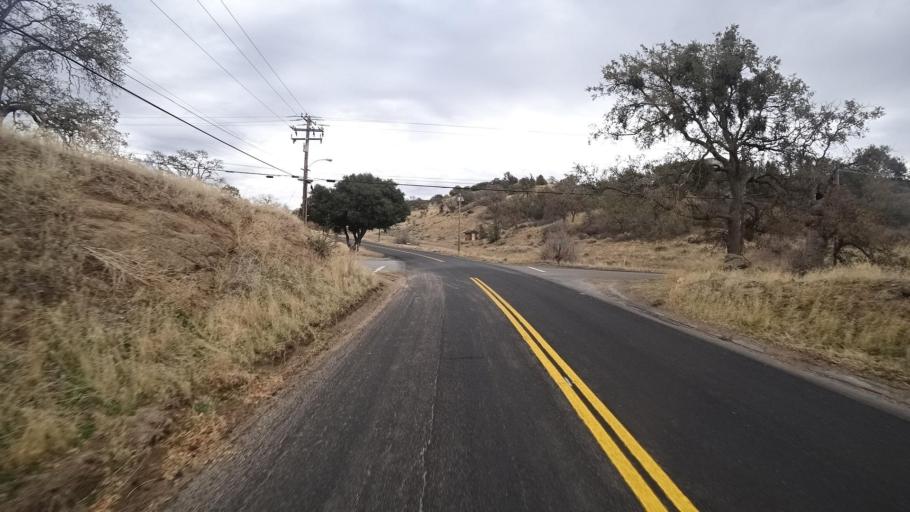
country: US
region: California
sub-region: Kern County
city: Stallion Springs
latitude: 35.0947
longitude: -118.6611
